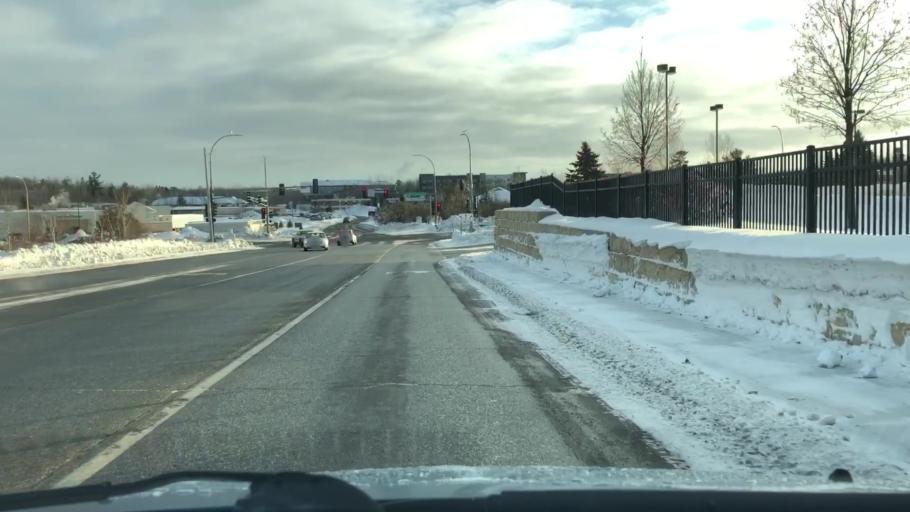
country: US
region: Minnesota
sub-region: Saint Louis County
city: Duluth
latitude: 46.8086
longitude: -92.1694
